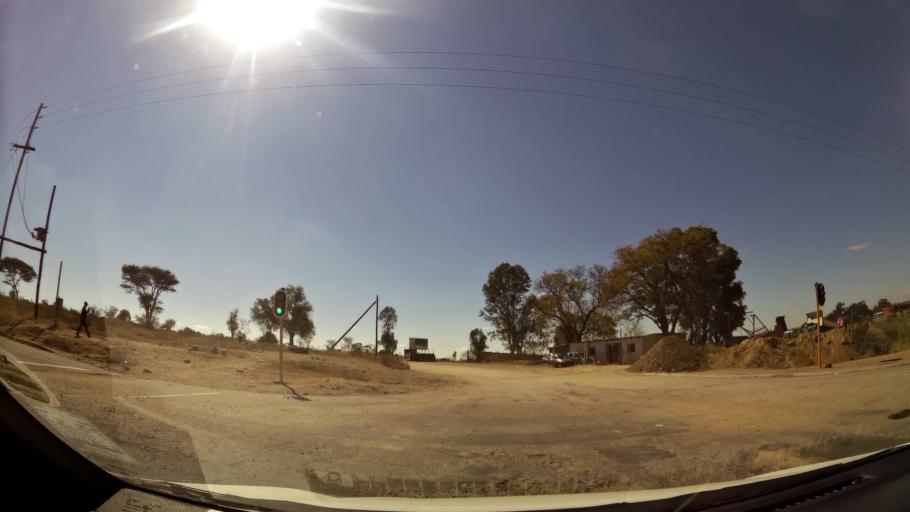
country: ZA
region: Limpopo
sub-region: Capricorn District Municipality
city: Polokwane
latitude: -23.8837
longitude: 29.4248
